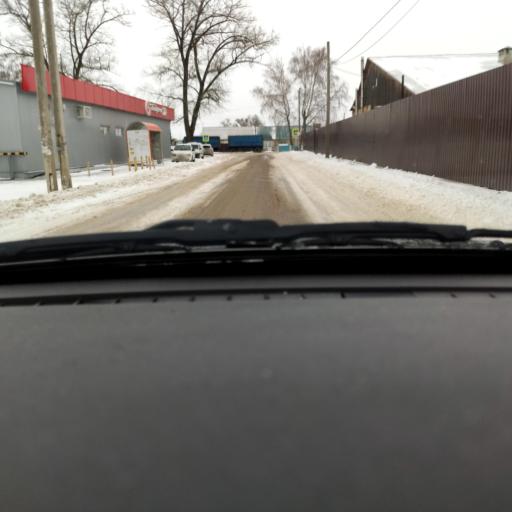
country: RU
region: Voronezj
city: Maslovka
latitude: 51.5388
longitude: 39.3417
